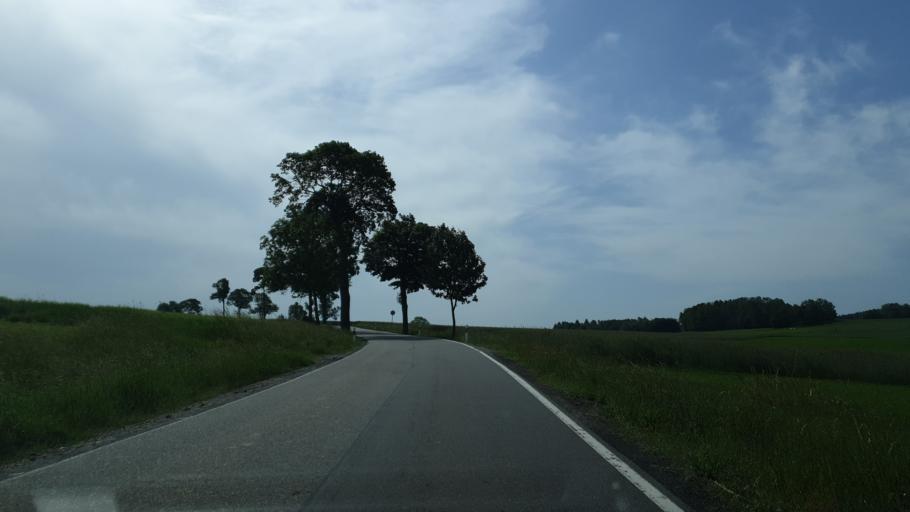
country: DE
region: Saxony
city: Zschorlau
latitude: 50.5579
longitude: 12.6470
